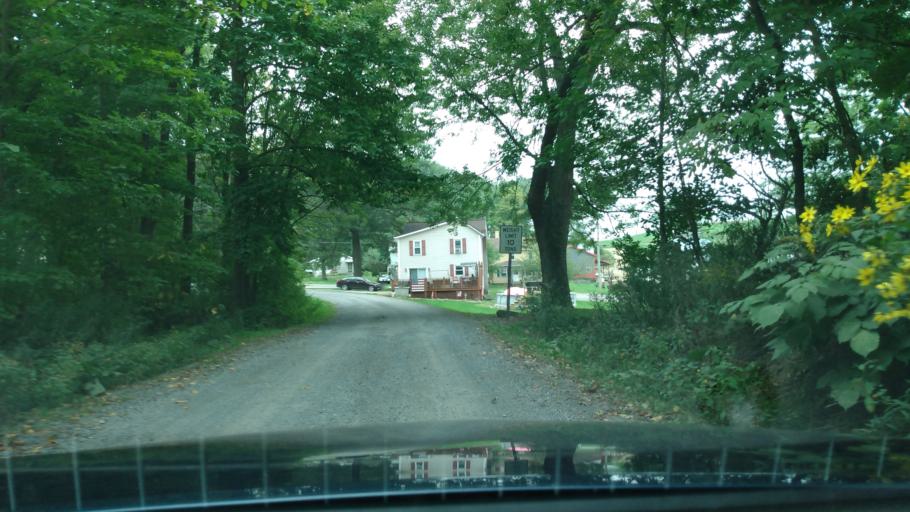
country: US
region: Pennsylvania
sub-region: Cambria County
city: Hastings
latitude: 40.6135
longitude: -78.7111
